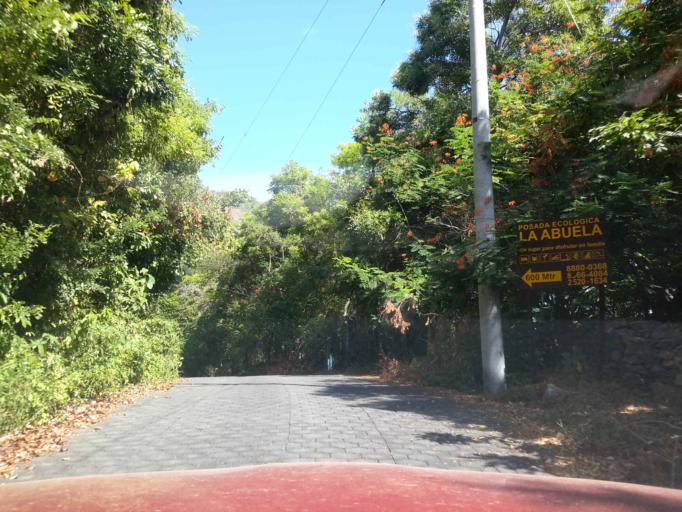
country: NI
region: Masaya
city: Catarina
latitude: 11.9400
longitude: -86.0496
